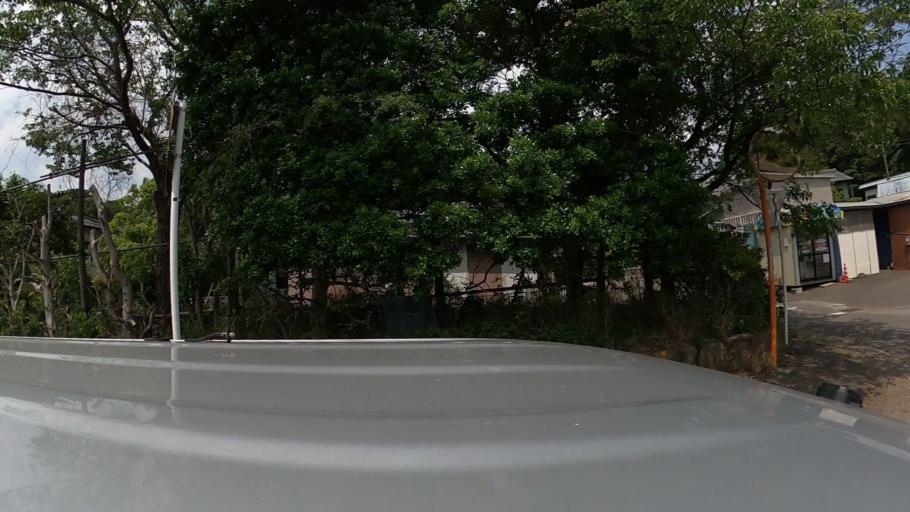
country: JP
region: Kanagawa
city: Chigasaki
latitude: 35.3848
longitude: 139.4232
